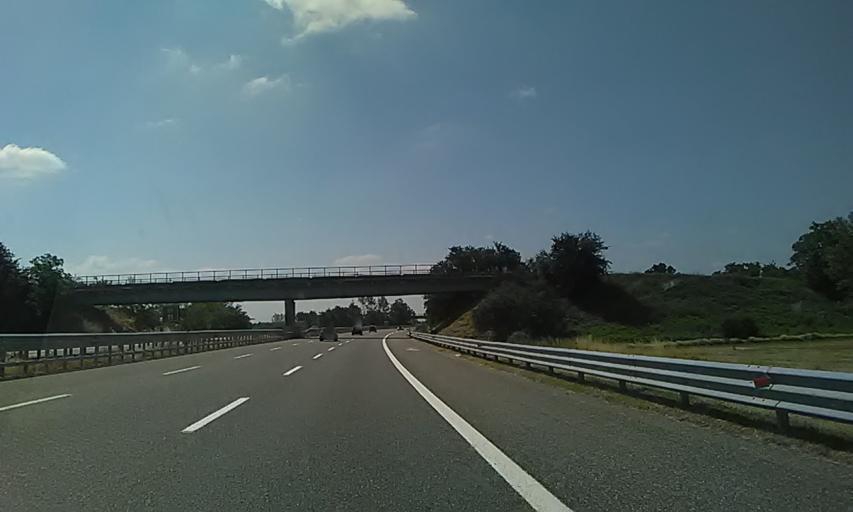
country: IT
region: Piedmont
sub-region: Provincia di Alessandria
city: Castellazzo Bormida
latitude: 44.8449
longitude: 8.5955
